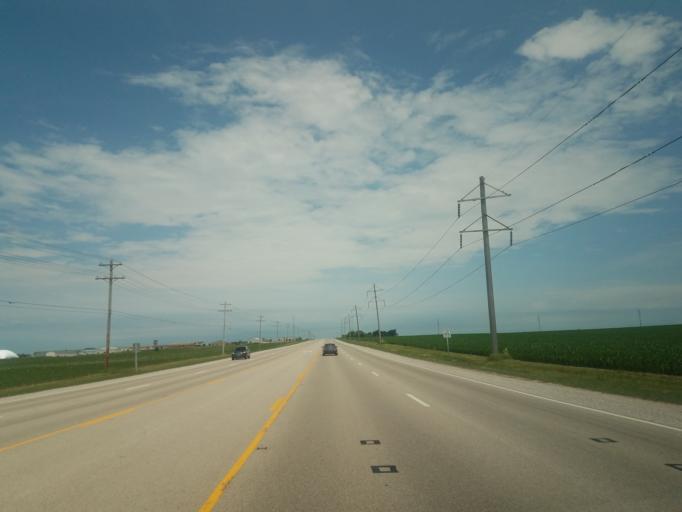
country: US
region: Illinois
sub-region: McLean County
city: Downs
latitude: 40.4608
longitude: -88.9019
